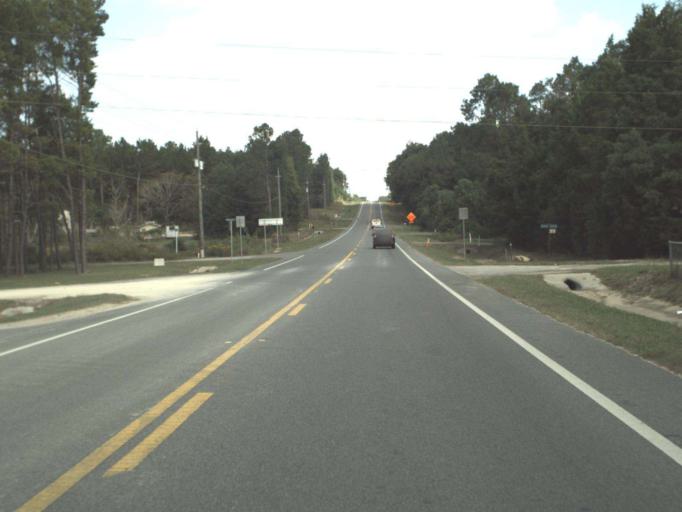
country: US
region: Florida
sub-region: Walton County
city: DeFuniak Springs
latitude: 30.7454
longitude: -86.1148
